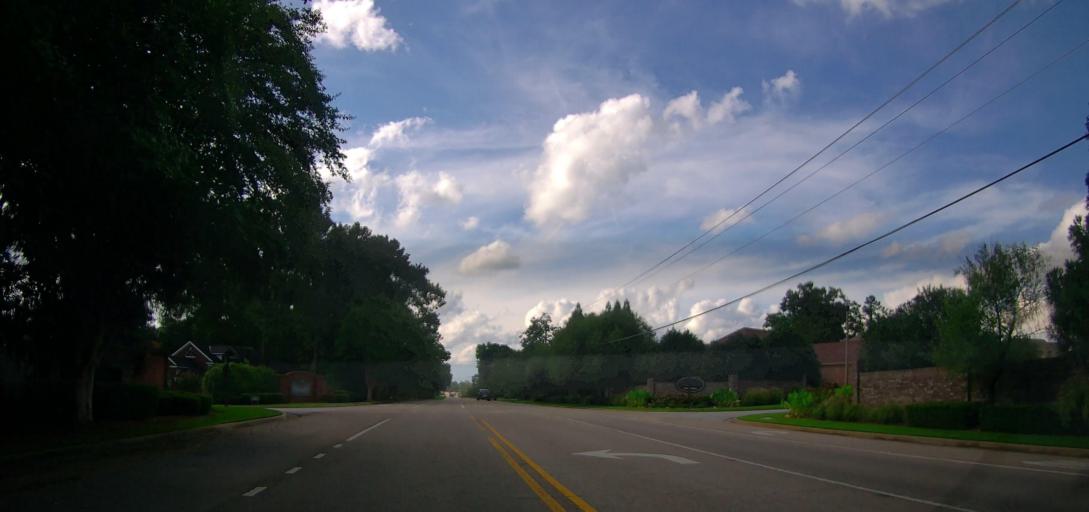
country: US
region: Alabama
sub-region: Russell County
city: Phenix City
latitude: 32.5154
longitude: -85.0244
